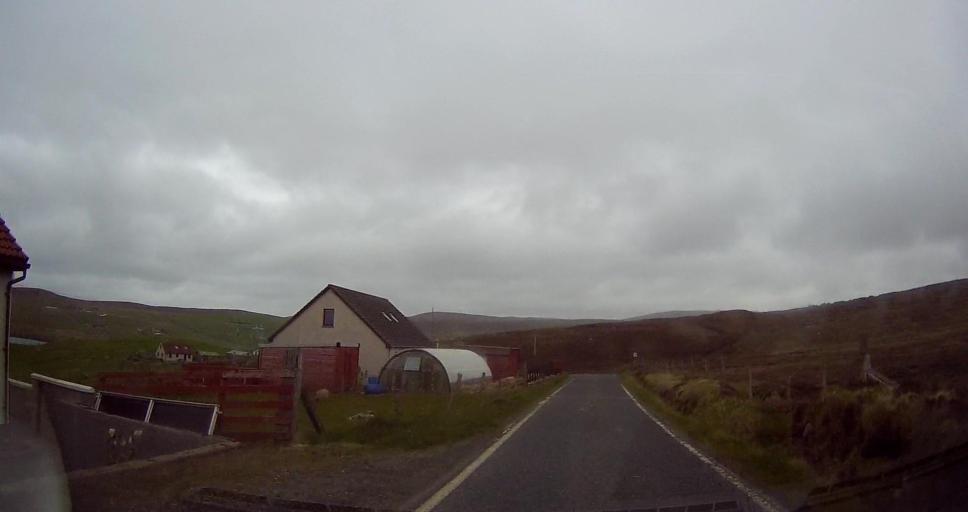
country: GB
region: Scotland
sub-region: Shetland Islands
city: Lerwick
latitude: 60.2974
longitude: -1.3624
